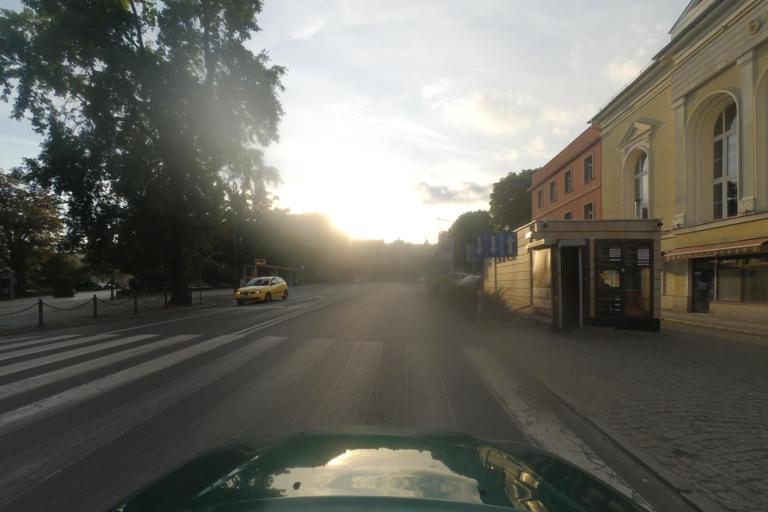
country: PL
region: Lower Silesian Voivodeship
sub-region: Powiat swidnicki
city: Swidnica
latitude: 50.8411
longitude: 16.4842
